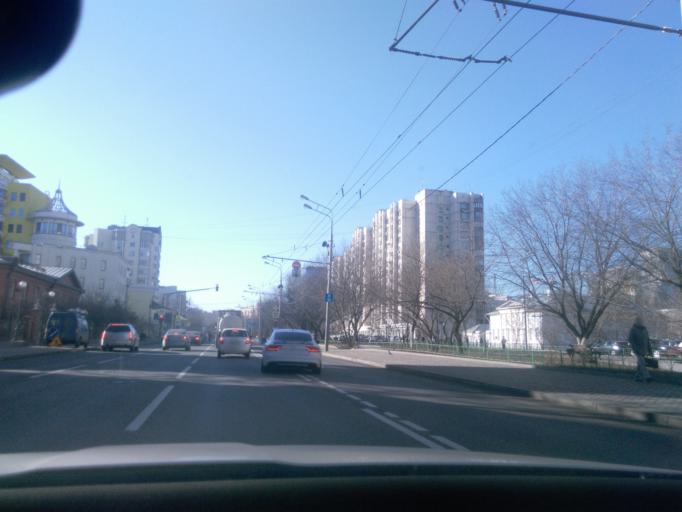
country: RU
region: Moscow
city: Zamoskvorech'ye
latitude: 55.7268
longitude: 37.6231
